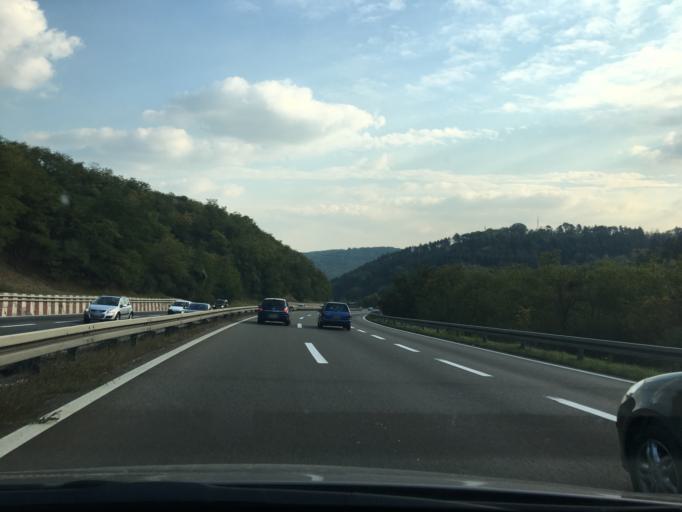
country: RS
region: Central Serbia
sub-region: Belgrade
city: Zvezdara
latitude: 44.7463
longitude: 20.5412
